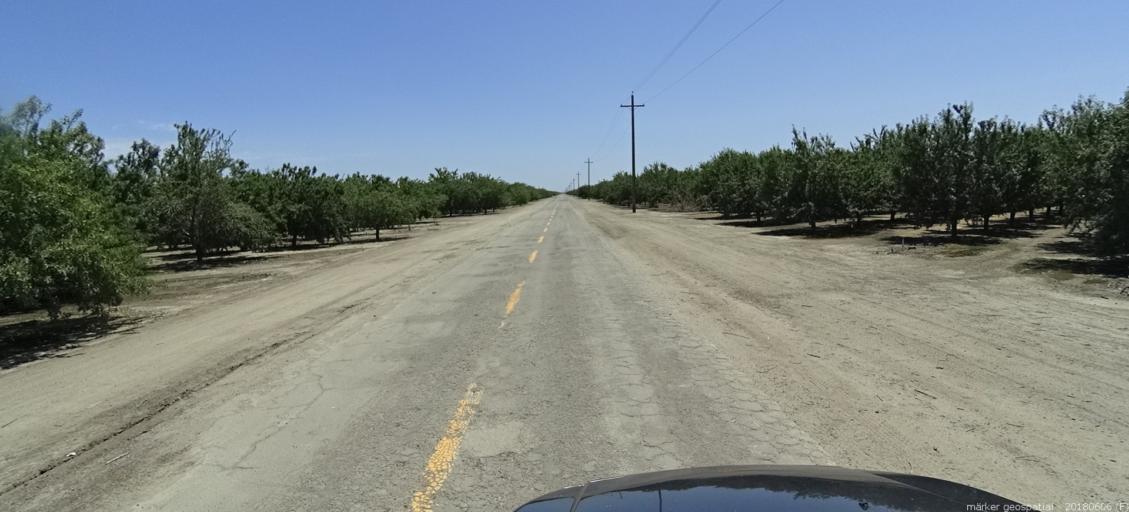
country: US
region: California
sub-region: Fresno County
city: Mendota
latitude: 36.8025
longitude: -120.3388
